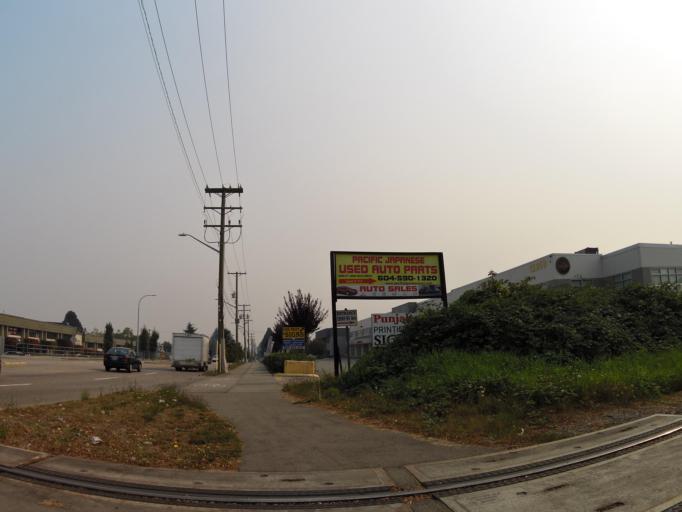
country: CA
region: British Columbia
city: Delta
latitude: 49.1480
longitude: -122.8646
